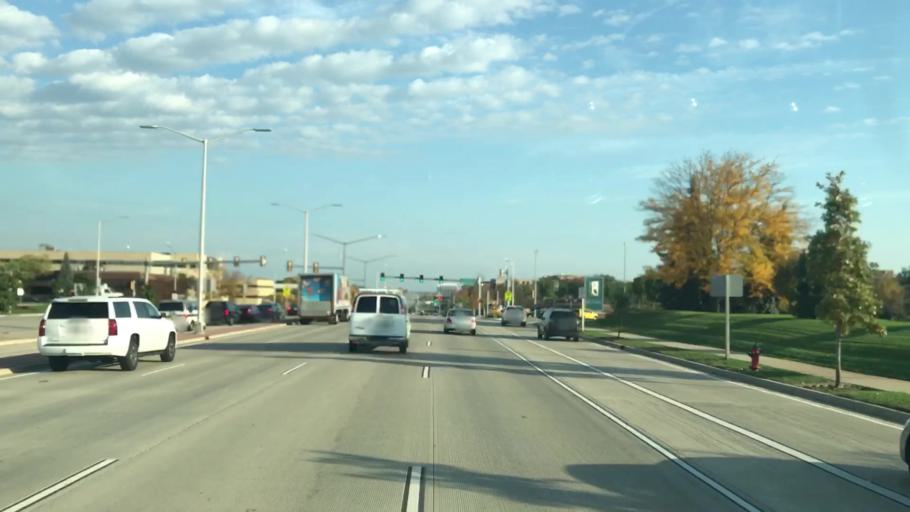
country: US
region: Wisconsin
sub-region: Waukesha County
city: Elm Grove
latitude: 43.0400
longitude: -88.0469
